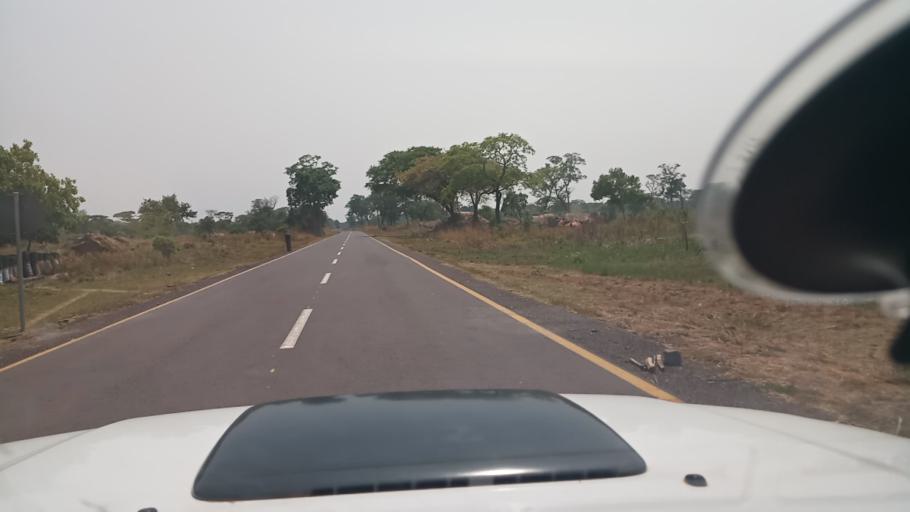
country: ZM
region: Luapula
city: Mwense
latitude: -10.7884
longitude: 28.2370
